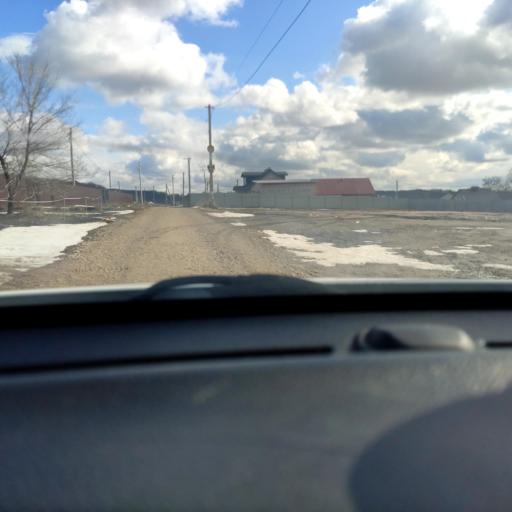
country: RU
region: Voronezj
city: Somovo
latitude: 51.6925
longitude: 39.3786
